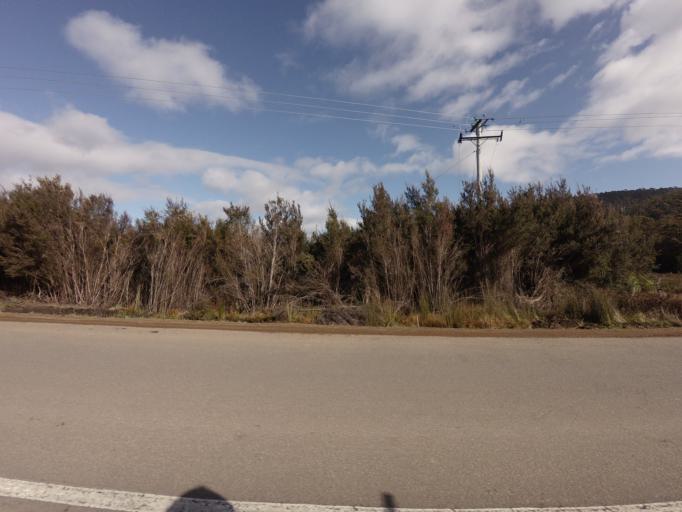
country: AU
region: Tasmania
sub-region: Huon Valley
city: Geeveston
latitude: -43.3277
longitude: 146.9709
